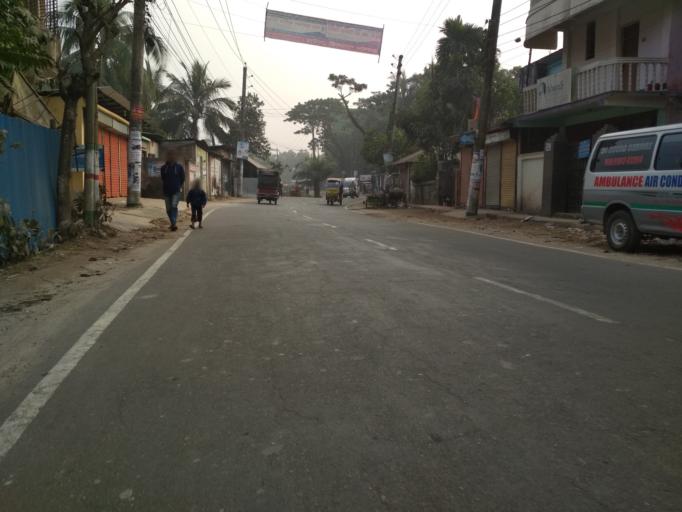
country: BD
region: Chittagong
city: Lakshmipur
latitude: 22.9390
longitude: 90.8415
